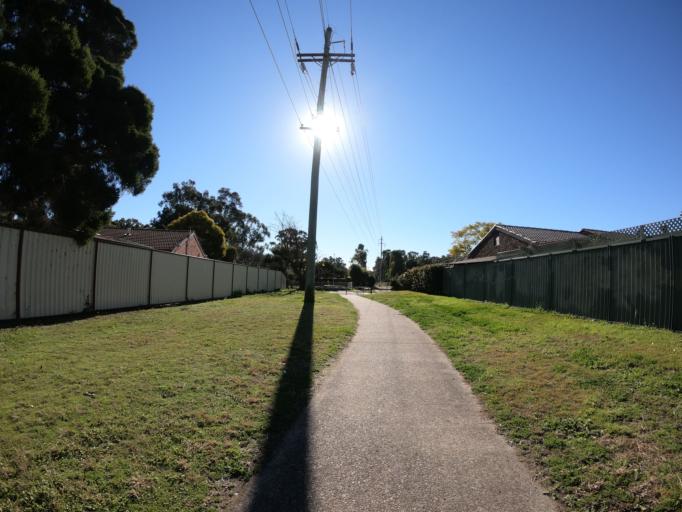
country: AU
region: New South Wales
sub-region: Hawkesbury
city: South Windsor
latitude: -33.6339
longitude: 150.7933
